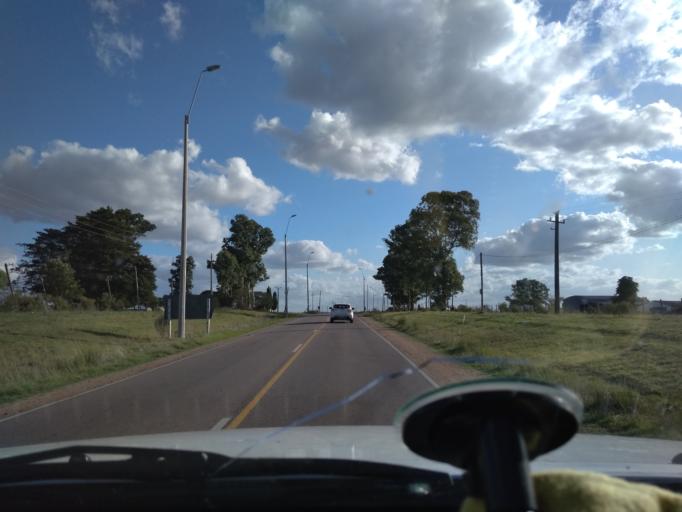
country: UY
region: Canelones
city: Tala
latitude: -34.3592
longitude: -55.7741
